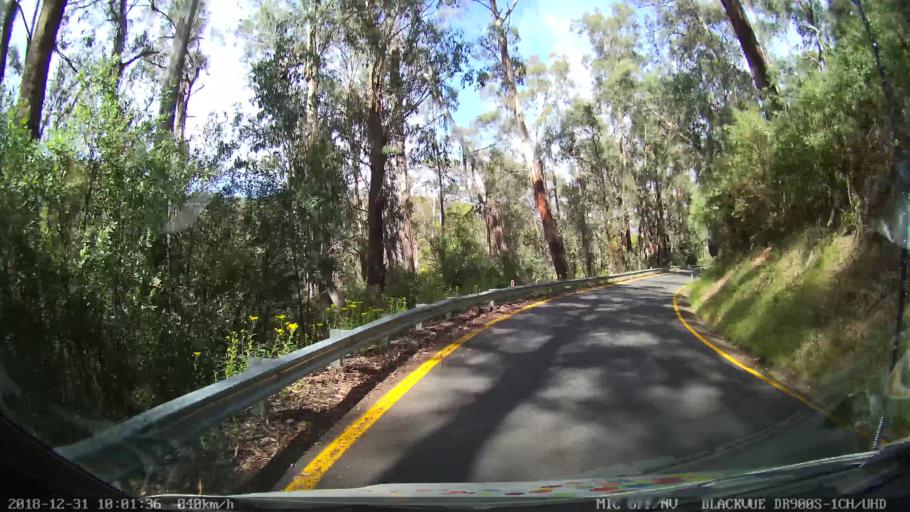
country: AU
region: New South Wales
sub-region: Snowy River
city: Jindabyne
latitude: -36.5322
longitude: 148.2027
